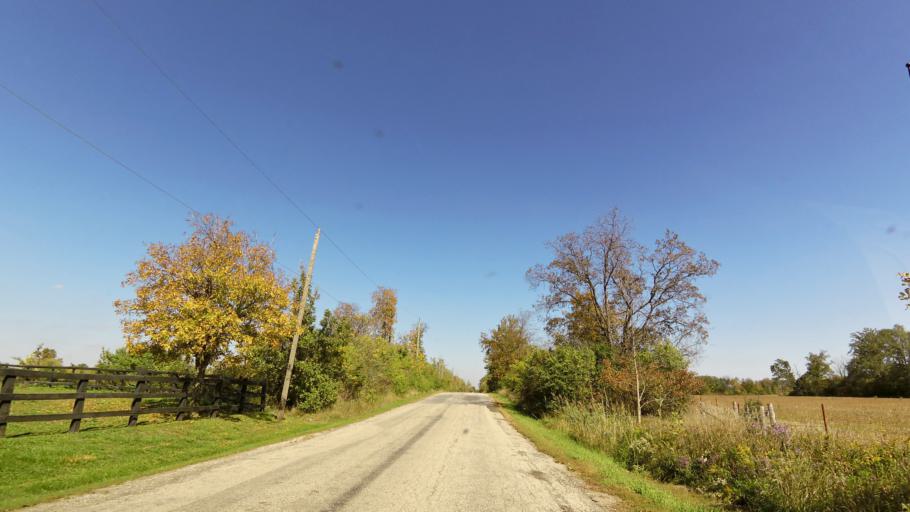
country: CA
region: Ontario
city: Burlington
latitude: 43.4509
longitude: -79.7935
